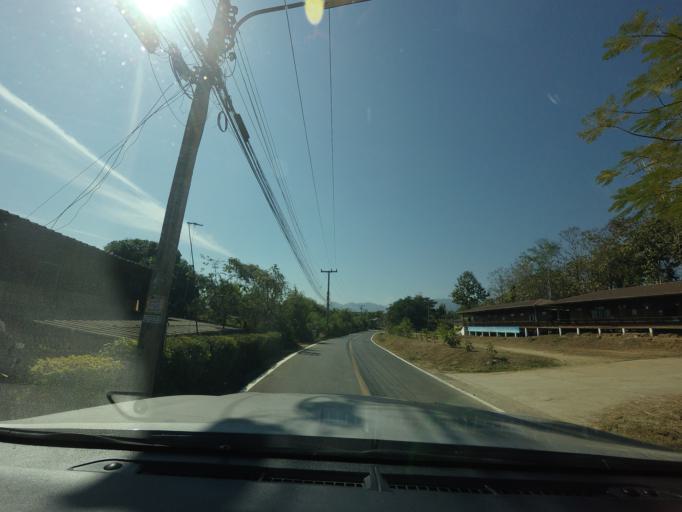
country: TH
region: Mae Hong Son
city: Wiang Nuea
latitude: 19.3841
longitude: 98.4388
